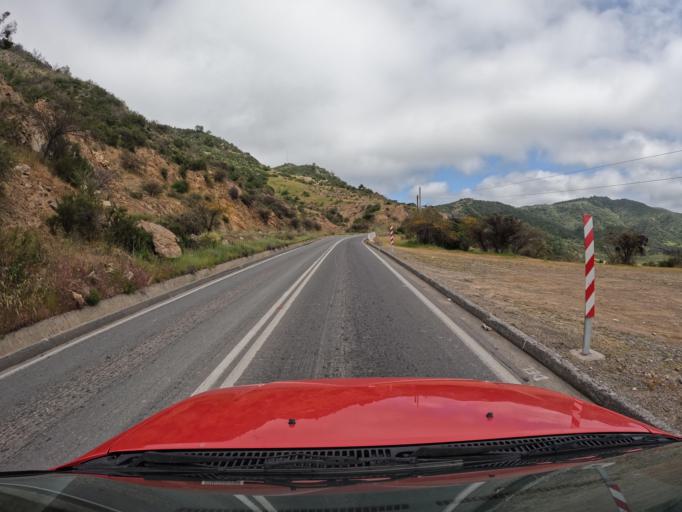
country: CL
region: O'Higgins
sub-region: Provincia de Colchagua
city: Santa Cruz
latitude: -34.6629
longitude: -71.4170
